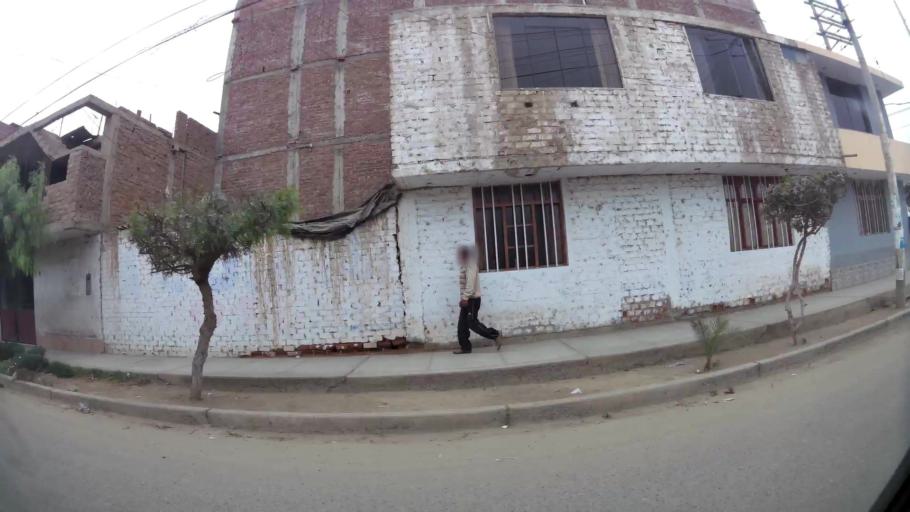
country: PE
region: La Libertad
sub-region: Provincia de Trujillo
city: Buenos Aires
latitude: -8.1409
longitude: -79.0467
